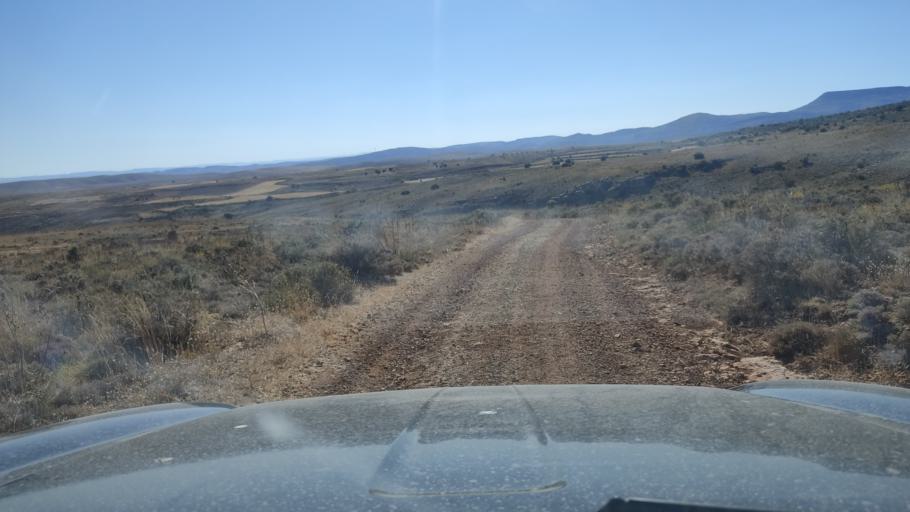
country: ES
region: Aragon
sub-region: Provincia de Teruel
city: Monforte de Moyuela
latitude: 41.0280
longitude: -1.0024
